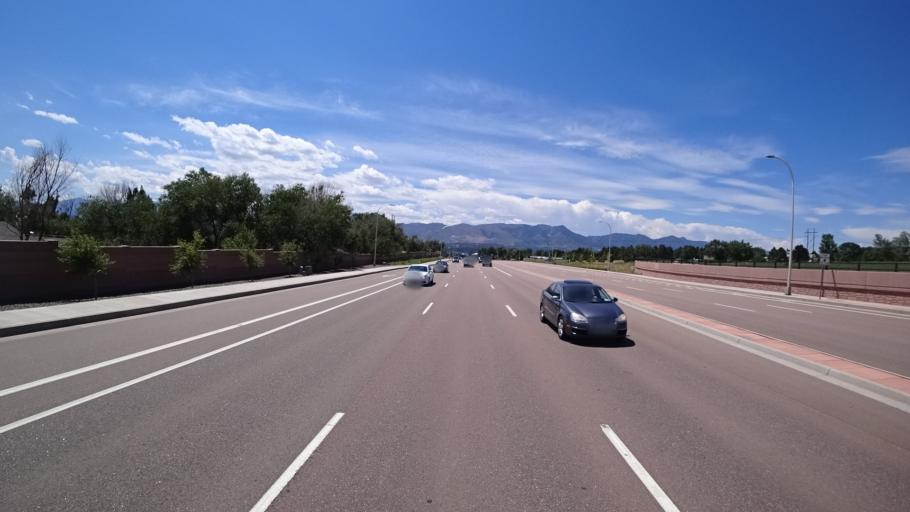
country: US
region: Colorado
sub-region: El Paso County
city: Air Force Academy
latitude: 38.9331
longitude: -104.7826
